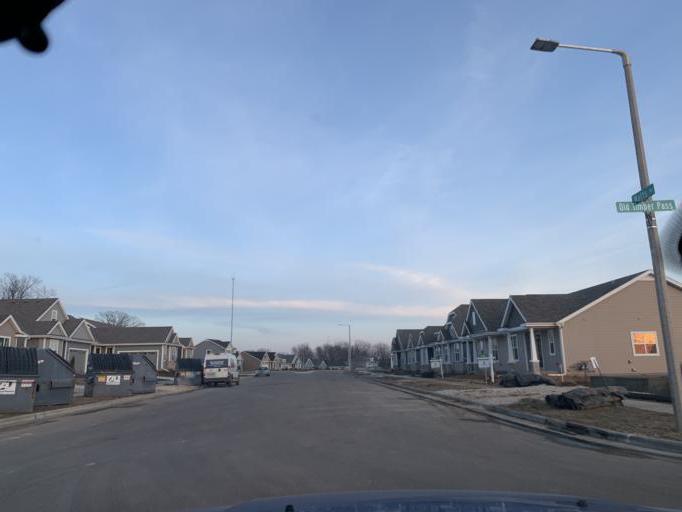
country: US
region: Wisconsin
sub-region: Dane County
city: Verona
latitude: 43.0524
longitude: -89.5645
